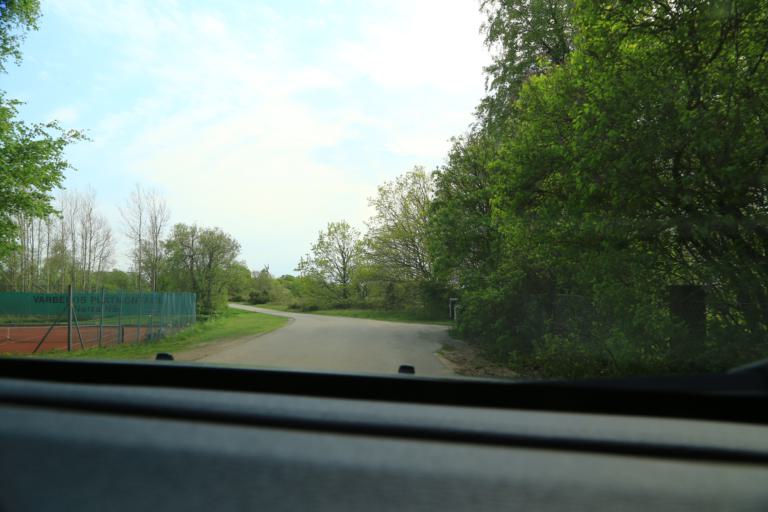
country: SE
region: Halland
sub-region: Varbergs Kommun
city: Varberg
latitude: 57.1447
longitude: 12.2274
